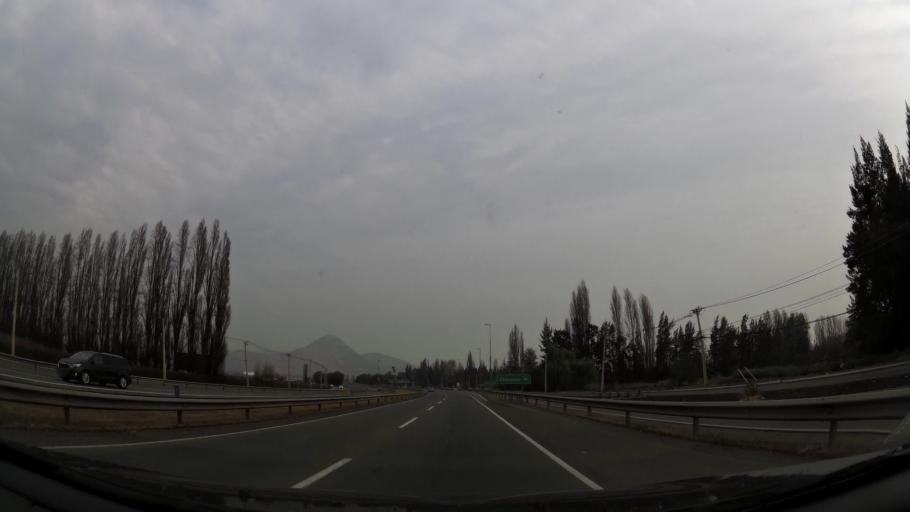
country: CL
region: Santiago Metropolitan
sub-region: Provincia de Chacabuco
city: Chicureo Abajo
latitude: -33.2798
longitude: -70.7031
